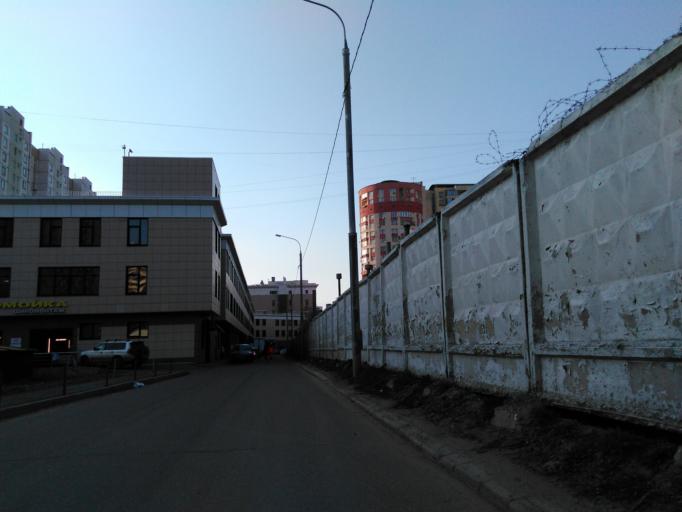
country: RU
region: Moscow
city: Ramenki
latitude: 55.6946
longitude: 37.5009
